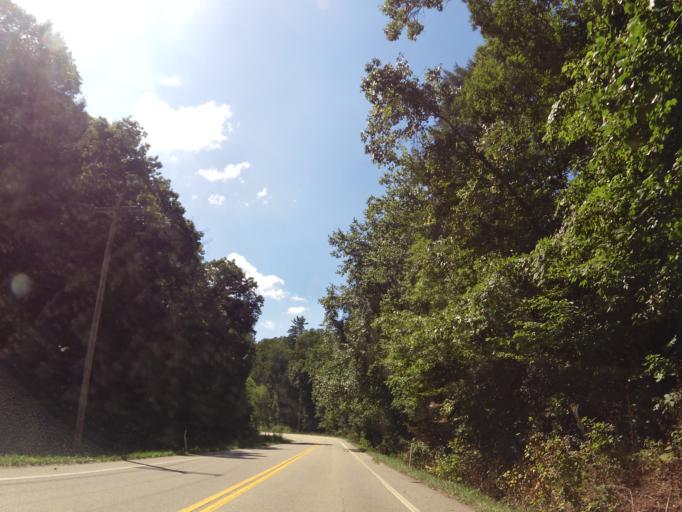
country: US
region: Tennessee
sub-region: Cumberland County
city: Fairfield Glade
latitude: 35.8857
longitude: -84.8323
